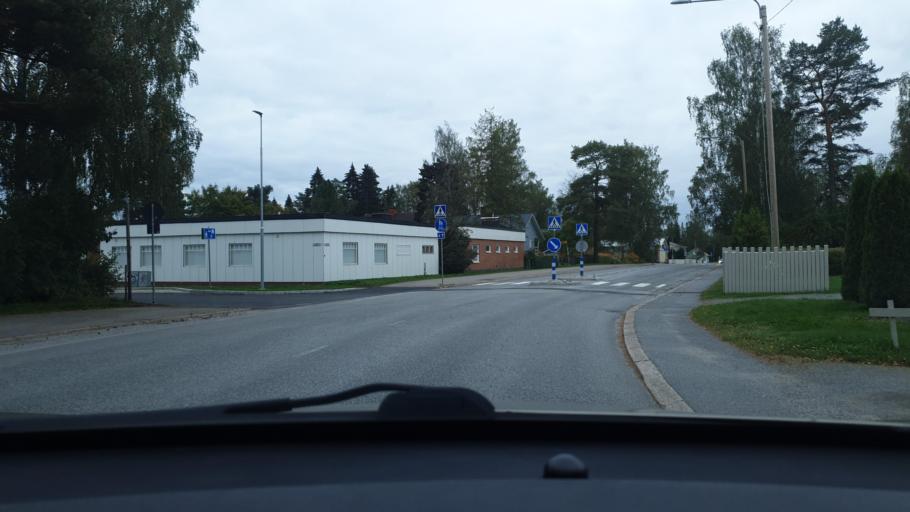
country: FI
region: Ostrobothnia
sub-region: Vaasa
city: Korsholm
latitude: 63.0968
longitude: 21.6691
